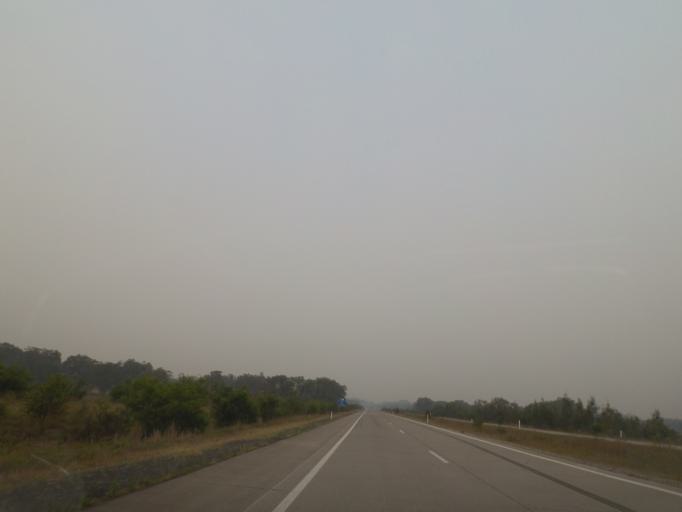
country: AU
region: New South Wales
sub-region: Kempsey
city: Frederickton
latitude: -30.9150
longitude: 152.9027
